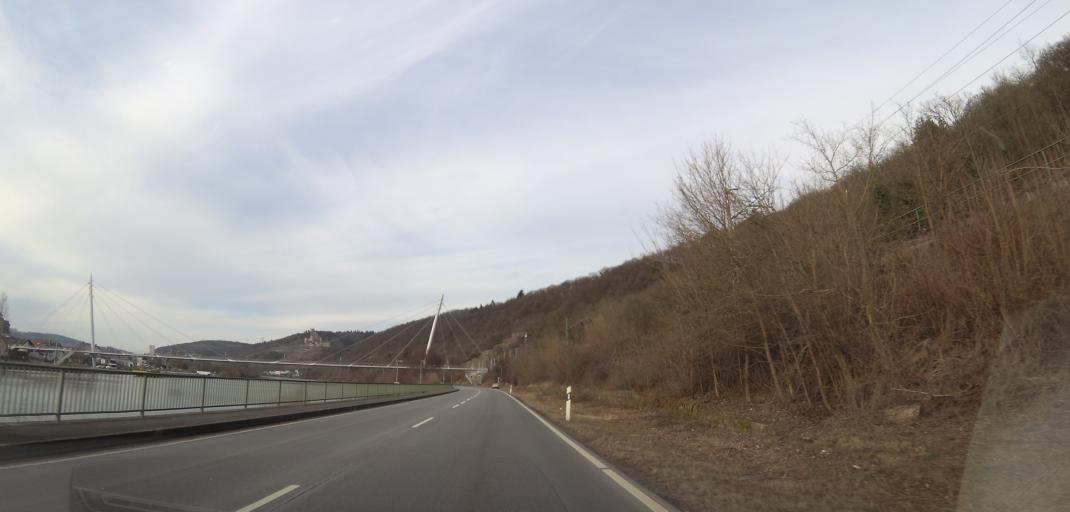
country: DE
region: Baden-Wuerttemberg
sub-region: Karlsruhe Region
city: Hassmersheim
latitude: 49.3020
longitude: 9.1543
